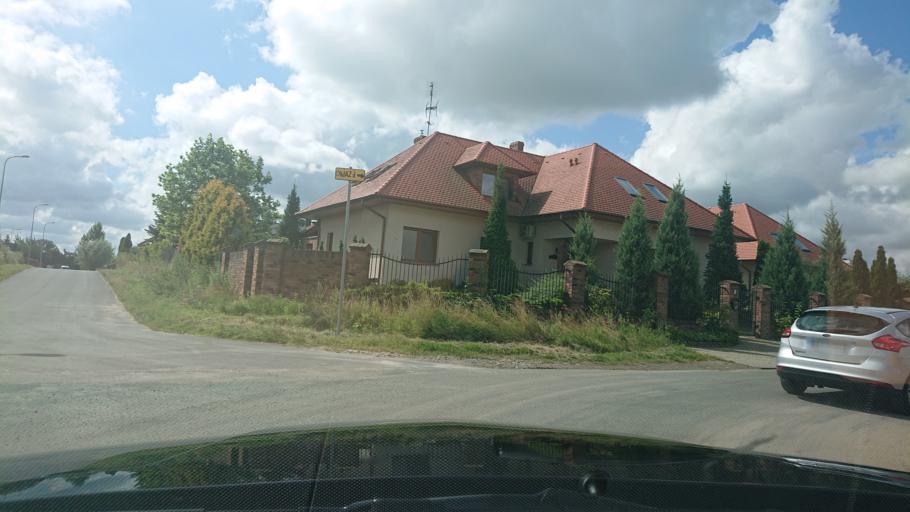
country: PL
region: Greater Poland Voivodeship
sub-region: Powiat gnieznienski
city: Gniezno
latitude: 52.5458
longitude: 17.6305
